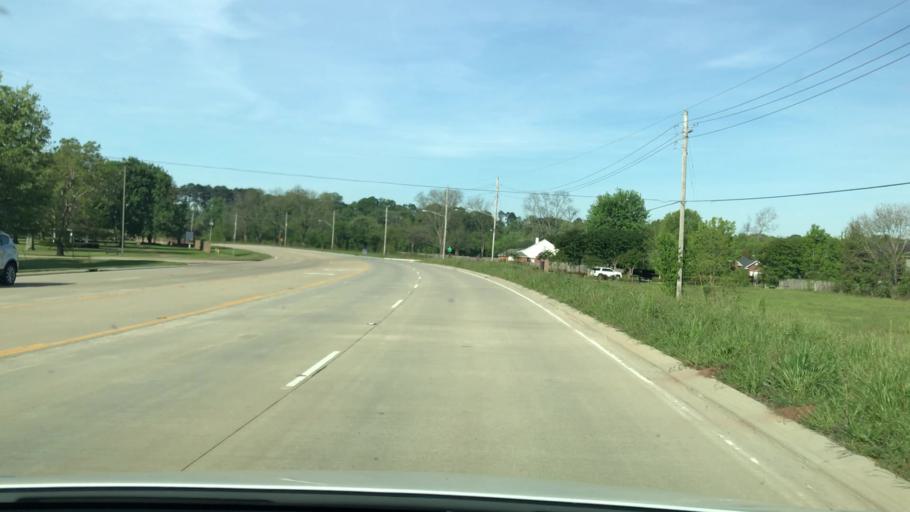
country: US
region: Louisiana
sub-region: Bossier Parish
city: Bossier City
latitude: 32.3999
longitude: -93.7192
